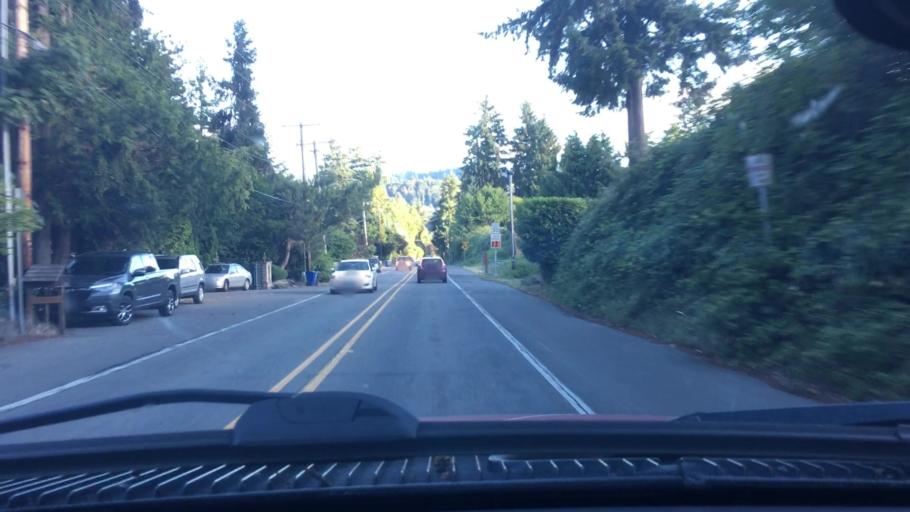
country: US
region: Washington
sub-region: King County
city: West Lake Sammamish
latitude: 47.5883
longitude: -122.1117
